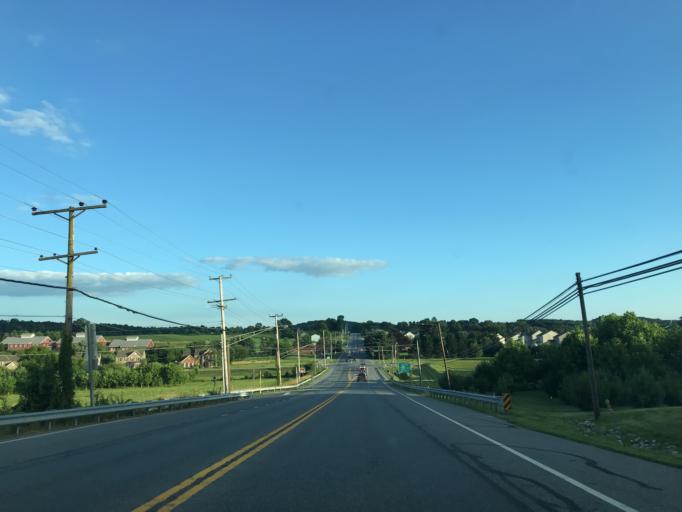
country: US
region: Maryland
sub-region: Carroll County
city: Manchester
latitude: 39.6810
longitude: -76.8918
